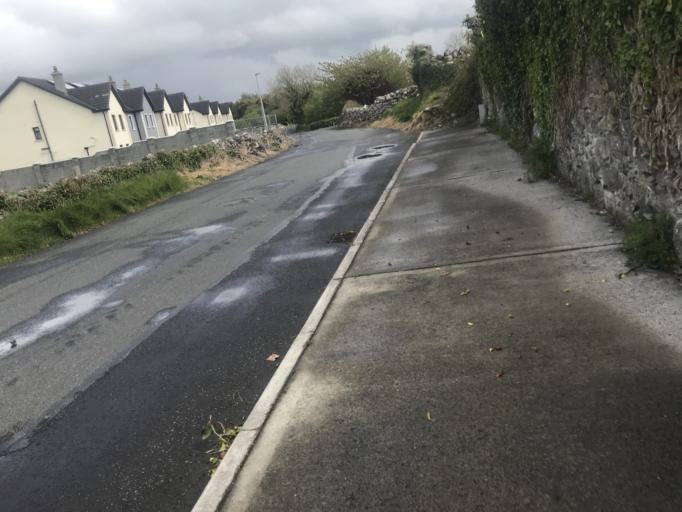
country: IE
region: Connaught
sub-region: County Galway
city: Moycullen
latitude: 53.4684
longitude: -9.0999
